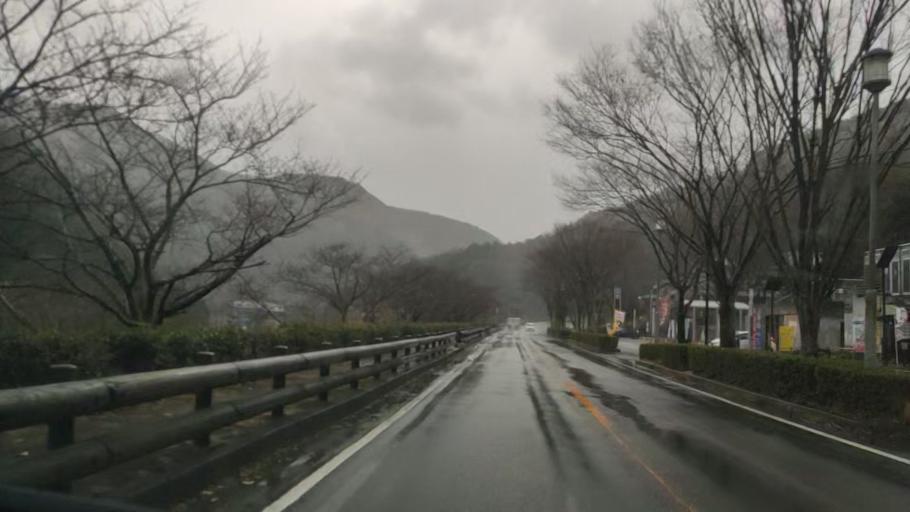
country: JP
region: Tokushima
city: Kamojimacho-jogejima
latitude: 34.1513
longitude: 134.3527
